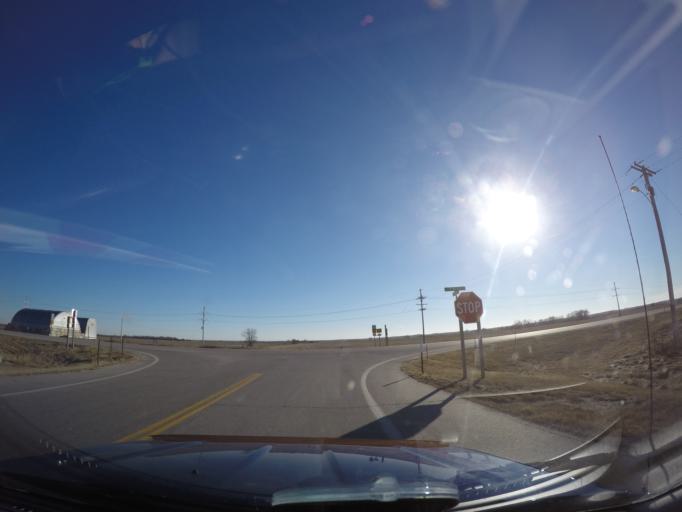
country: US
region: Kansas
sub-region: Marion County
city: Hillsboro
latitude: 38.3627
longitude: -97.3076
